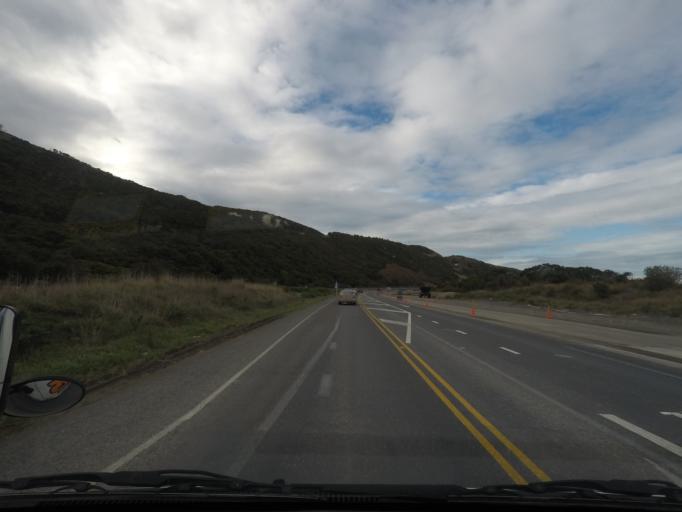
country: NZ
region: Canterbury
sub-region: Kaikoura District
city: Kaikoura
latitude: -42.2172
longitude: 173.8599
